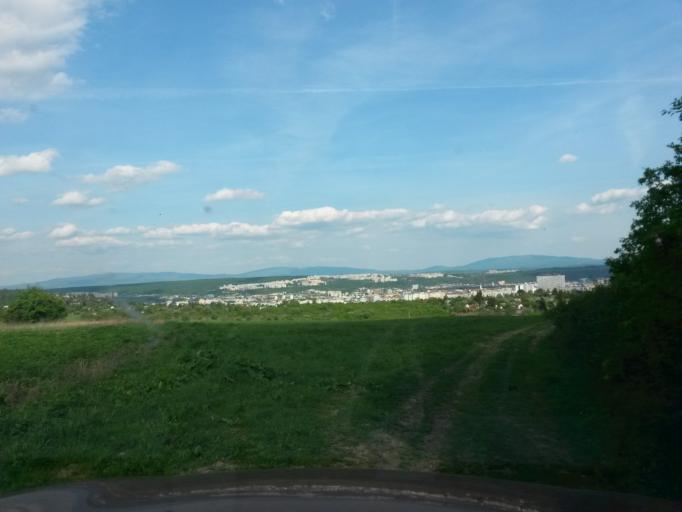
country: SK
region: Kosicky
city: Kosice
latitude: 48.7252
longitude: 21.2117
